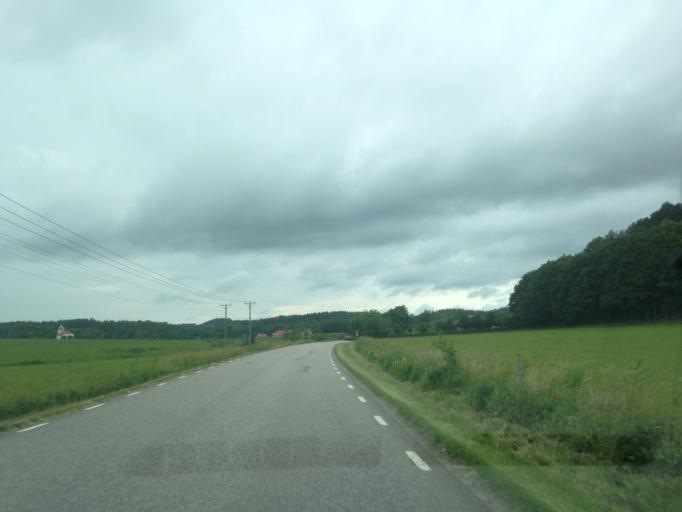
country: SE
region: Vaestra Goetaland
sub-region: Kungalvs Kommun
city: Kode
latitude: 57.8367
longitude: 11.7960
